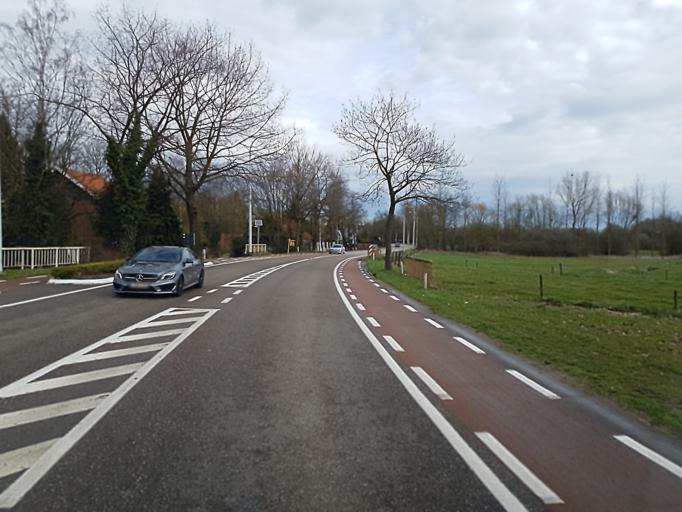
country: BE
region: Flanders
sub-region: Provincie Limburg
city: Kortessem
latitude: 50.8849
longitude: 5.3521
